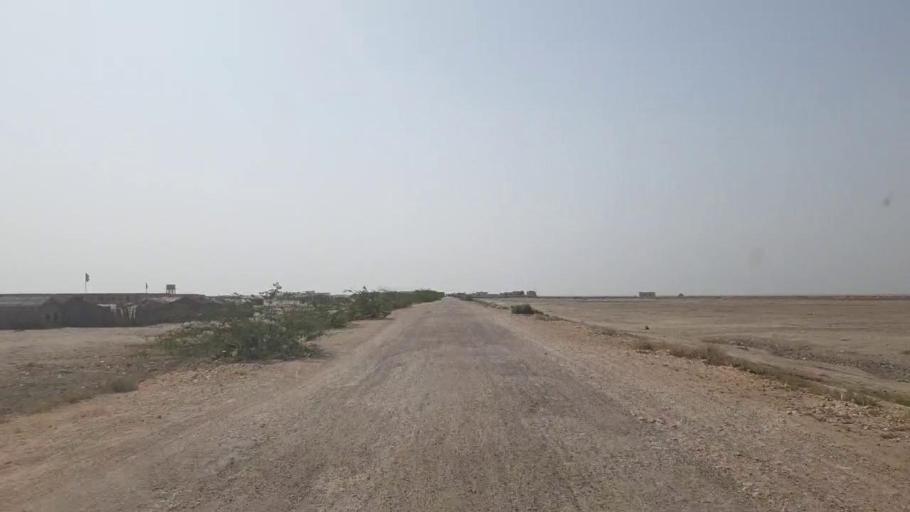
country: PK
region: Sindh
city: Jati
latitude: 24.3408
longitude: 68.5932
